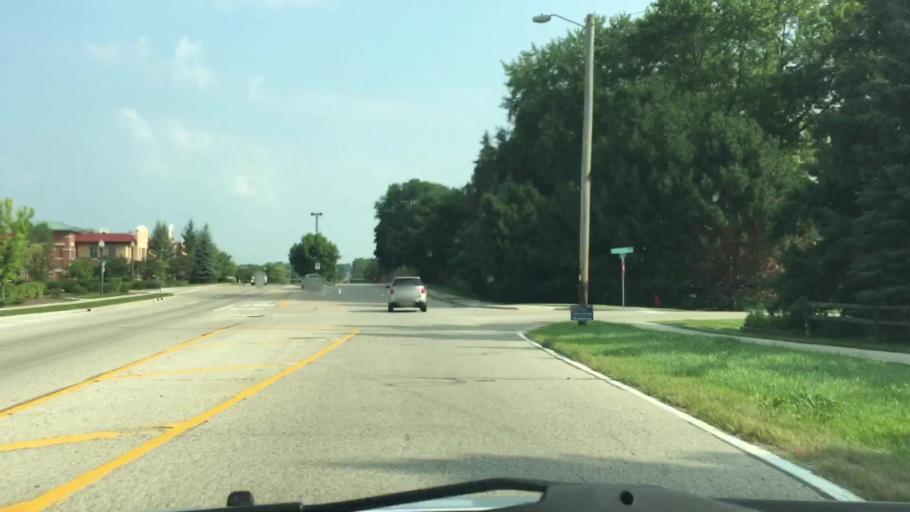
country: US
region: Wisconsin
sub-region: Waukesha County
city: Brookfield
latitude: 43.0866
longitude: -88.1456
